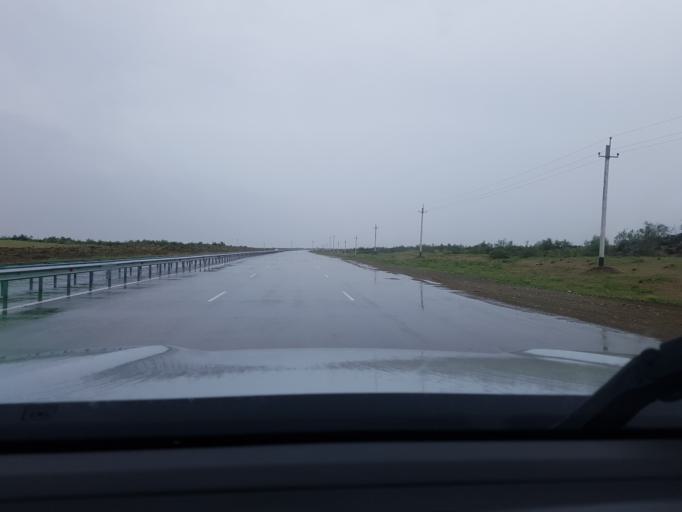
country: TM
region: Lebap
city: Farap
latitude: 39.2077
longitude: 63.6884
